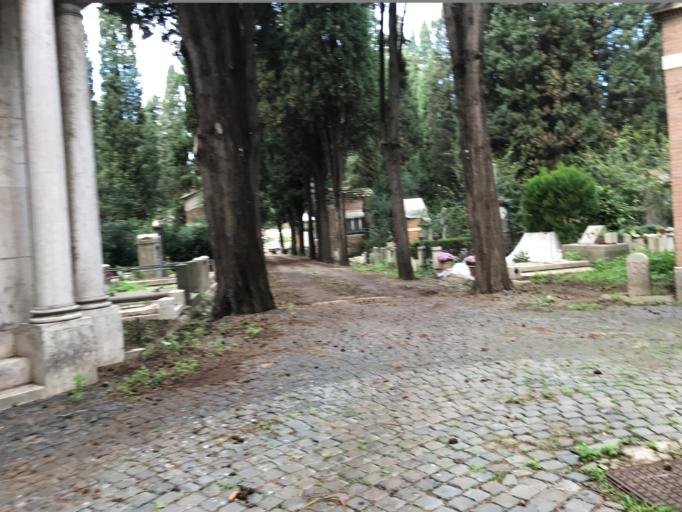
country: IT
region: Latium
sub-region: Citta metropolitana di Roma Capitale
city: Rome
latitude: 41.9060
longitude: 12.5251
